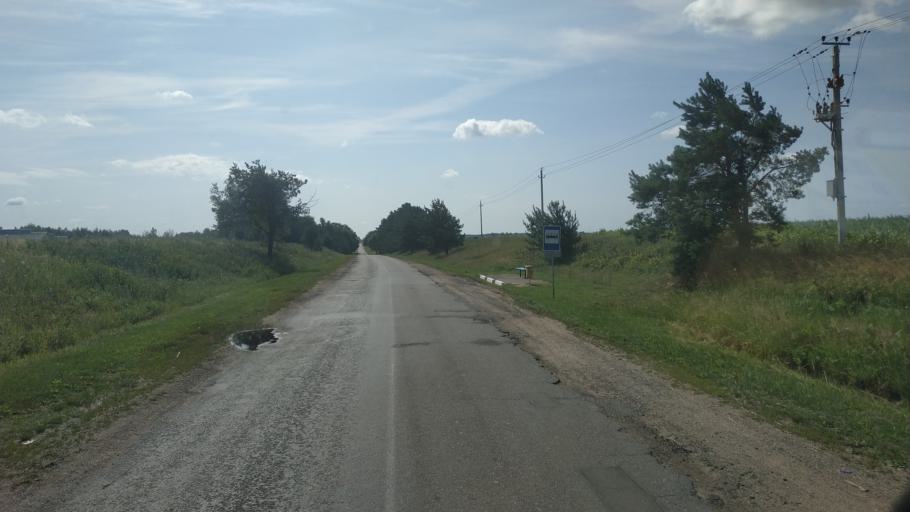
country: BY
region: Mogilev
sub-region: Mahilyowski Rayon
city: Veyno
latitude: 53.7841
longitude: 30.4363
